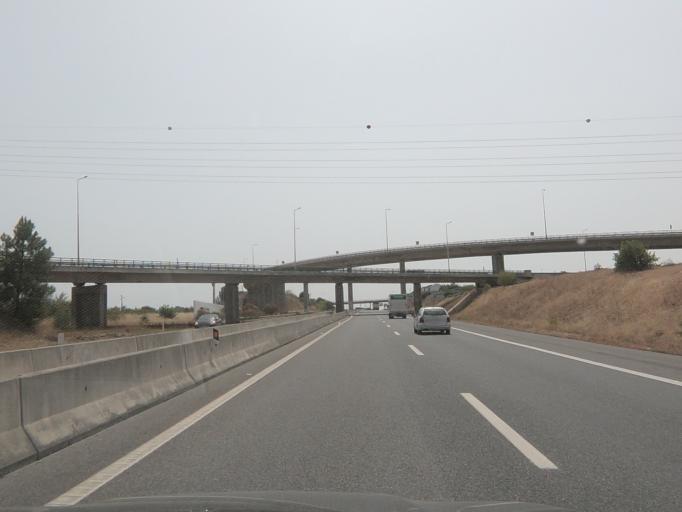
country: PT
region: Faro
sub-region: Albufeira
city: Ferreiras
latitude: 37.1554
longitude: -8.2086
